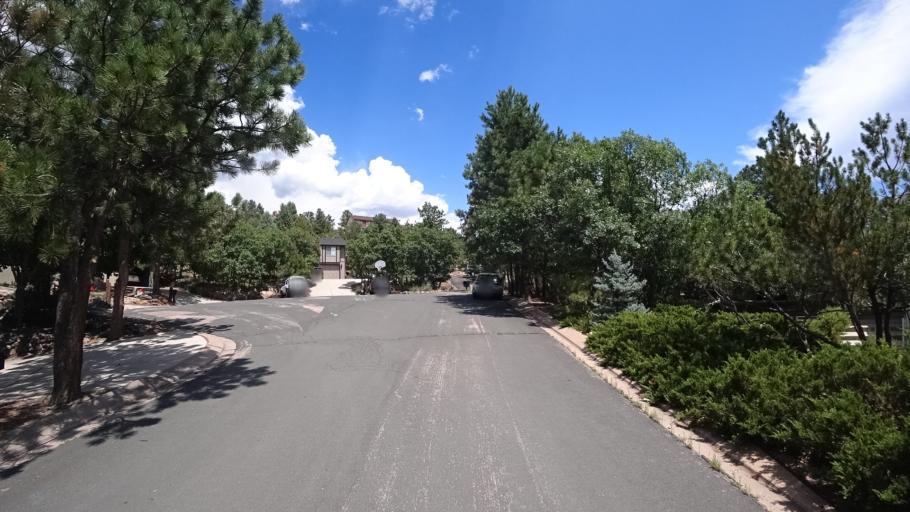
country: US
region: Colorado
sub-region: El Paso County
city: Air Force Academy
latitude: 38.9385
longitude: -104.8485
